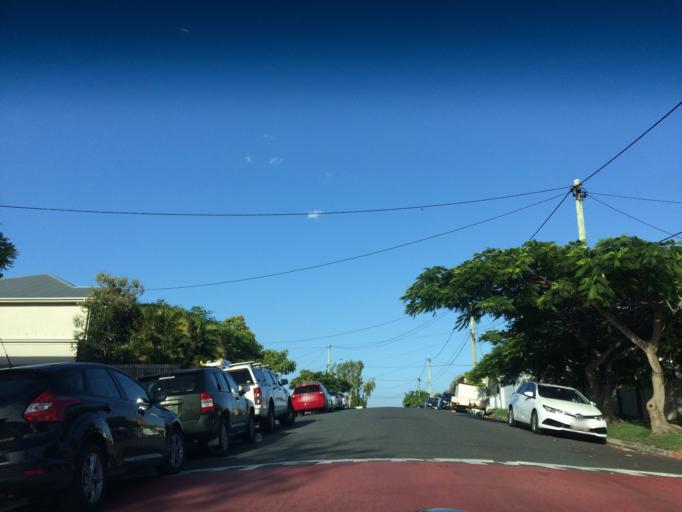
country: AU
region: Queensland
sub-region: Brisbane
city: Greenslopes
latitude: -27.4944
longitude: 153.0502
